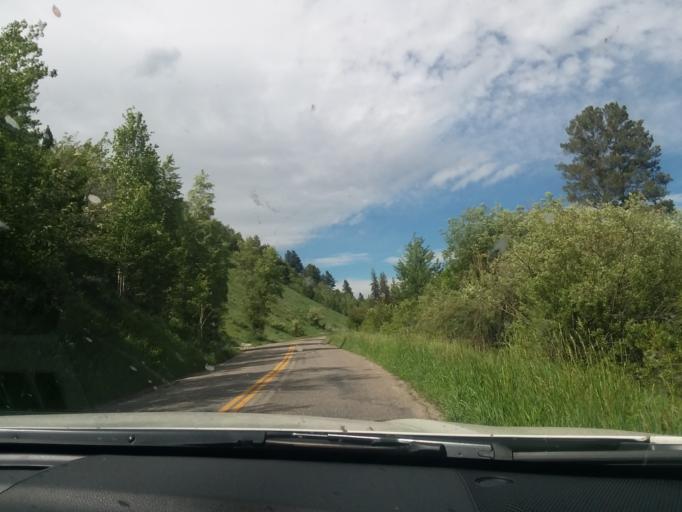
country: US
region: Wyoming
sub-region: Teton County
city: Moose Wilson Road
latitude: 43.5236
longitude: -110.8635
